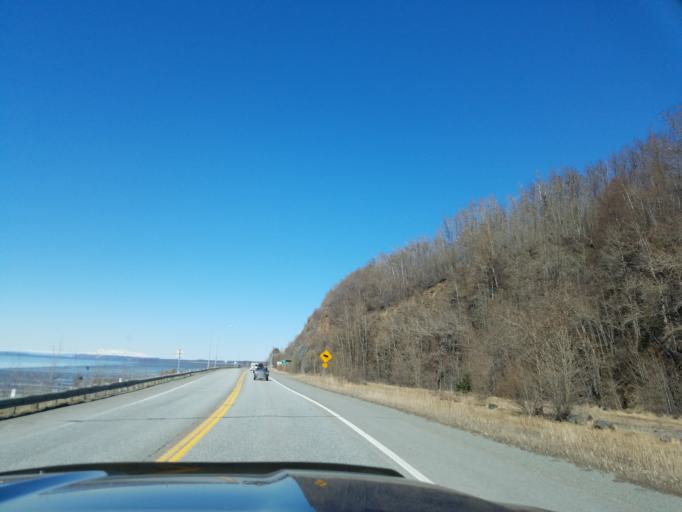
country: US
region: Alaska
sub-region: Anchorage Municipality
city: Anchorage
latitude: 61.0418
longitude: -149.7850
